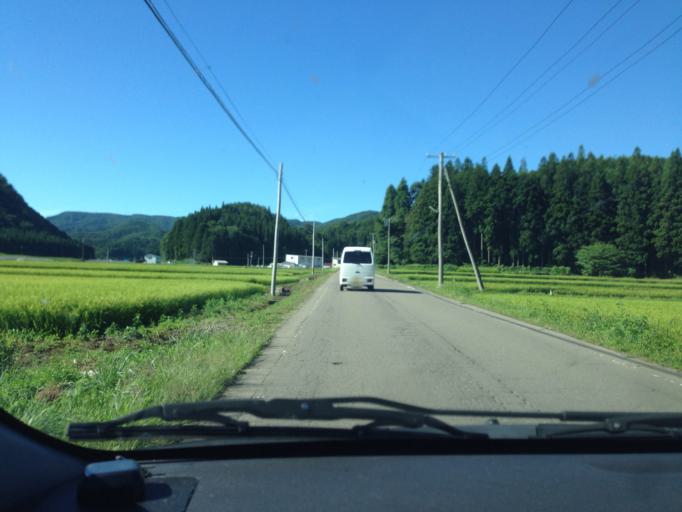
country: JP
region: Fukushima
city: Inawashiro
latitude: 37.3948
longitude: 140.0677
